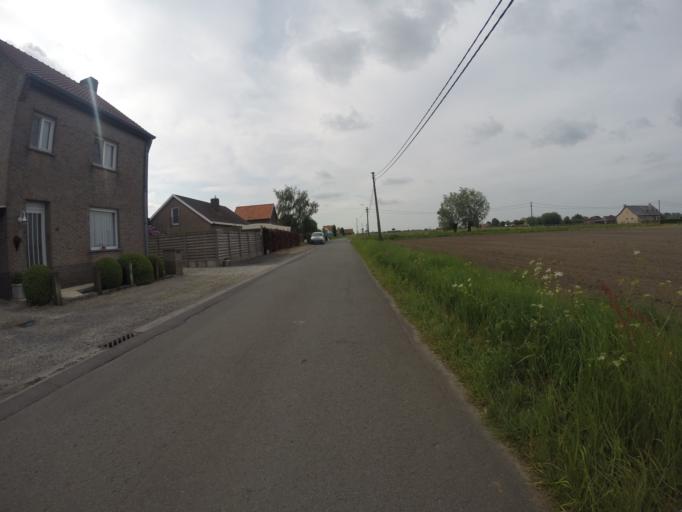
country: BE
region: Flanders
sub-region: Provincie West-Vlaanderen
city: Wingene
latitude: 51.0613
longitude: 3.3257
